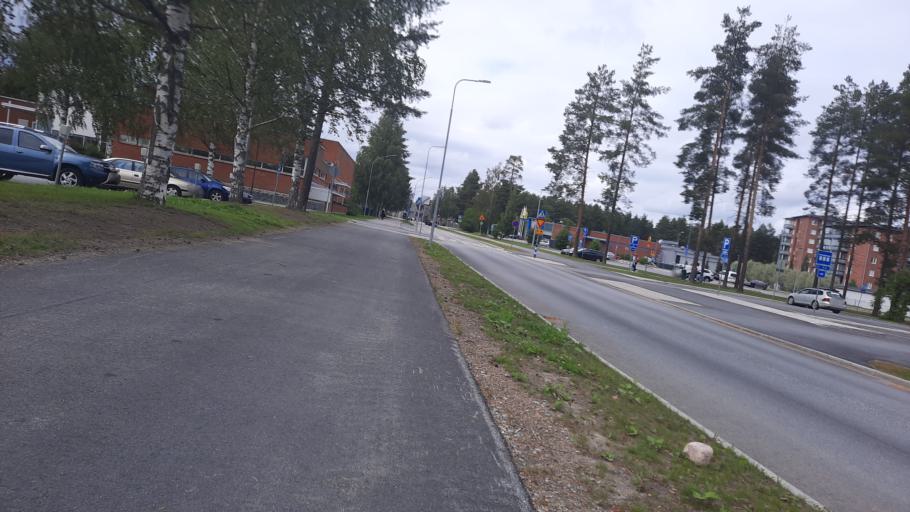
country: FI
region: North Karelia
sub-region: Joensuu
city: Joensuu
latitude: 62.6139
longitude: 29.8214
